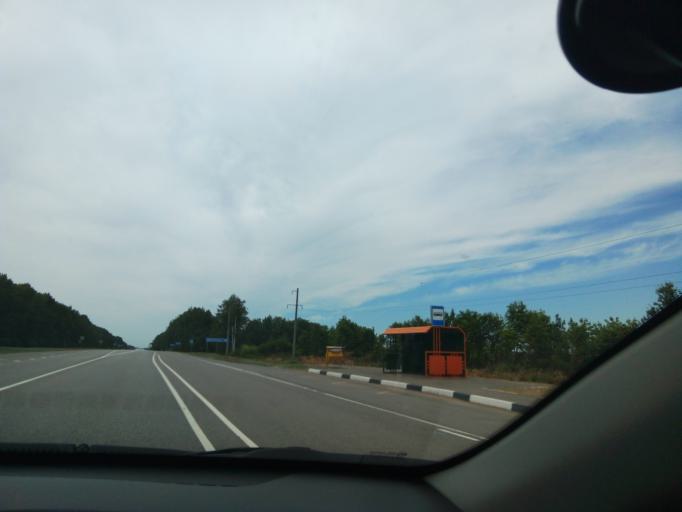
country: RU
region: Tambov
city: Selezni
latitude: 52.6689
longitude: 41.1043
